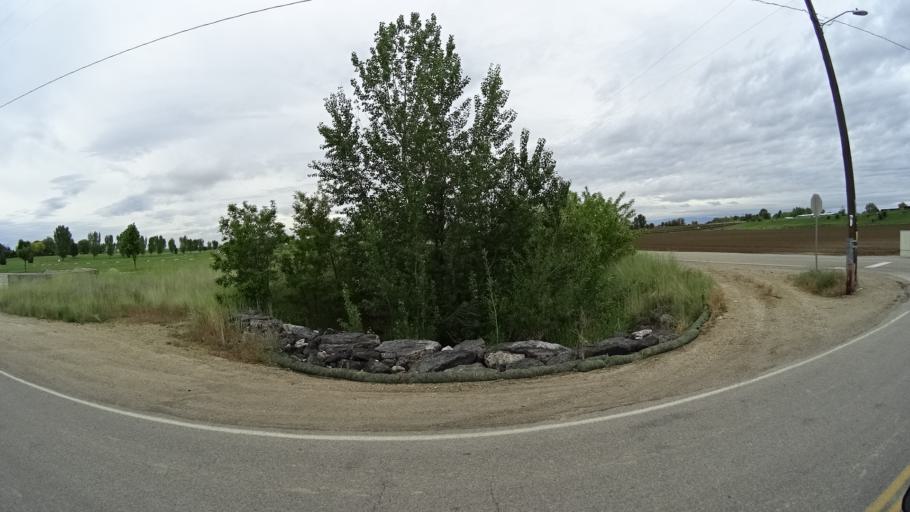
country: US
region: Idaho
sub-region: Ada County
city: Star
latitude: 43.7212
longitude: -116.4680
